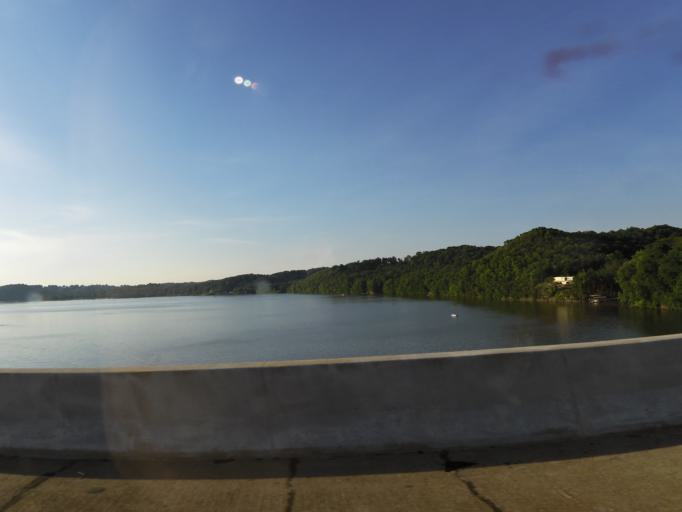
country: US
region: Tennessee
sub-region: Blount County
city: Louisville
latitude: 35.8498
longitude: -84.0089
